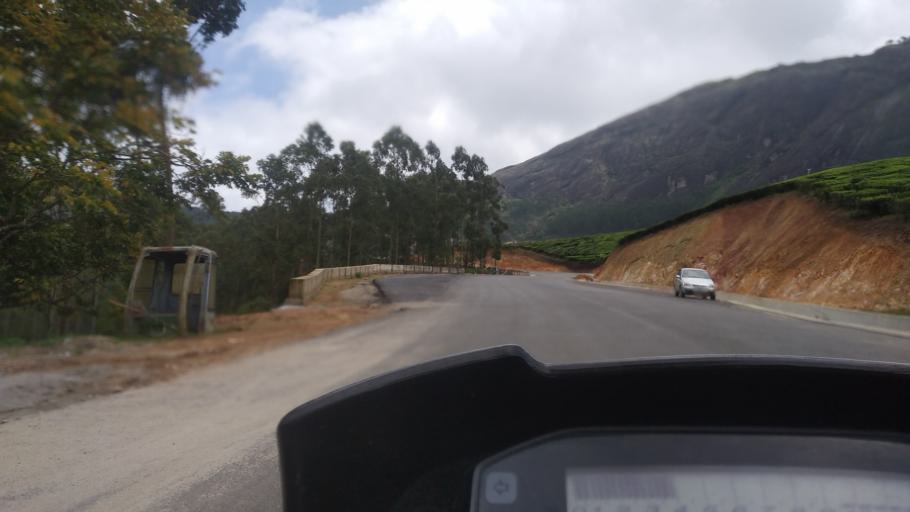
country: IN
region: Kerala
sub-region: Idukki
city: Munnar
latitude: 10.0474
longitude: 77.1137
